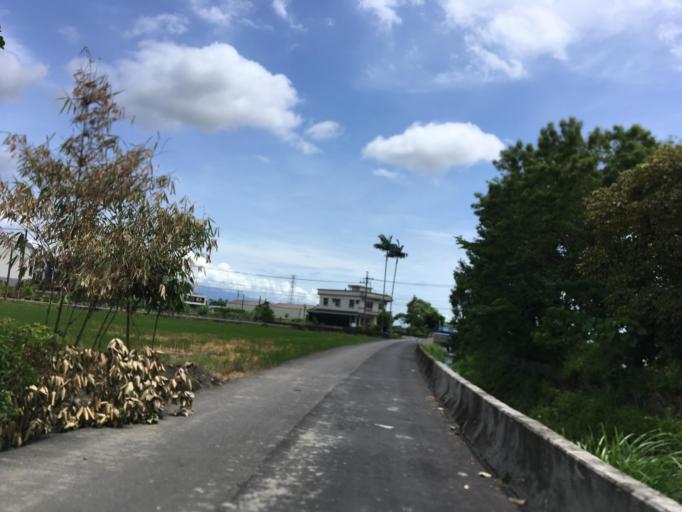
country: TW
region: Taiwan
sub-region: Yilan
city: Yilan
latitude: 24.6930
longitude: 121.7272
